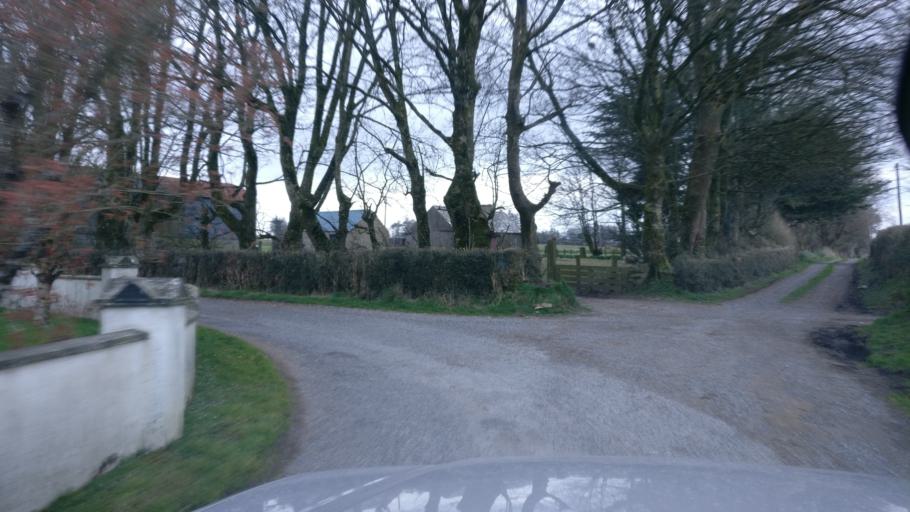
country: IE
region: Connaught
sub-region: County Galway
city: Loughrea
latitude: 53.2632
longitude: -8.4777
